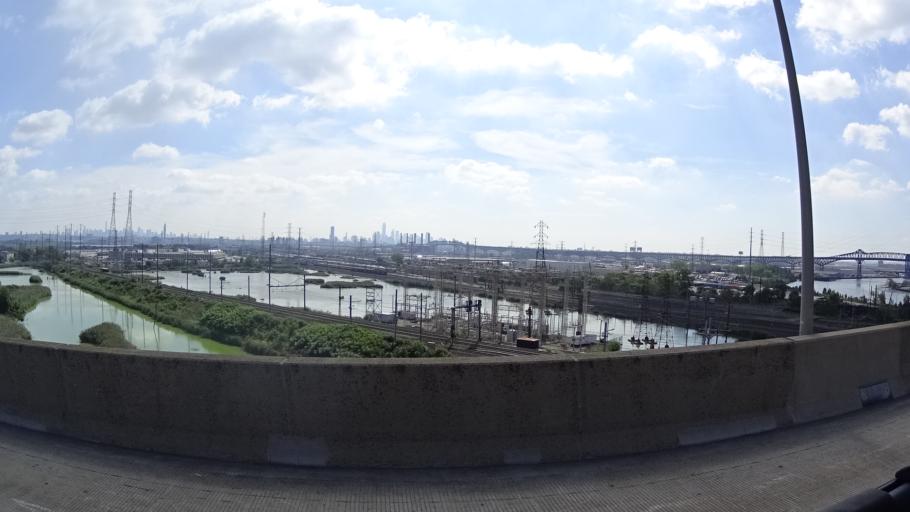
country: US
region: New Jersey
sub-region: Hudson County
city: Kearny
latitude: 40.7460
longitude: -74.1208
